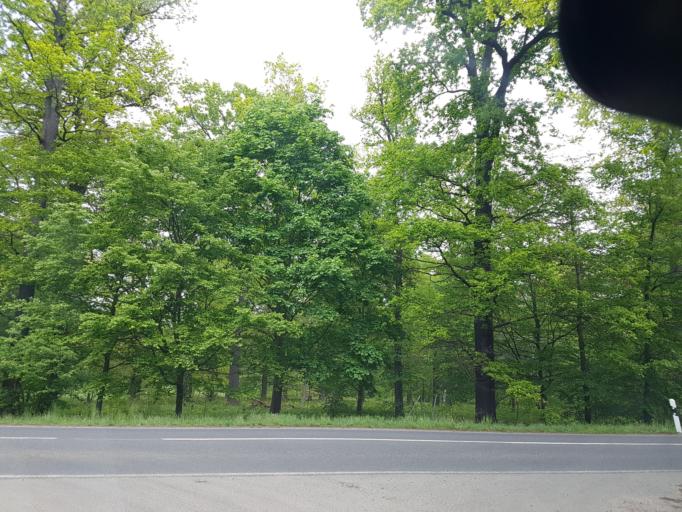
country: DE
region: Brandenburg
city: Altdobern
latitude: 51.6531
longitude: 14.0418
